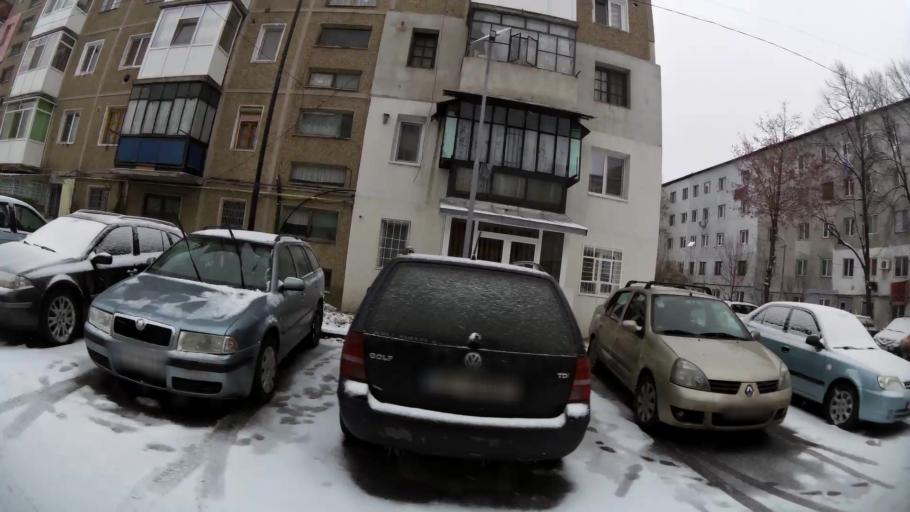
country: RO
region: Dambovita
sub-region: Municipiul Targoviste
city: Targoviste
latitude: 44.9242
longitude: 25.4486
